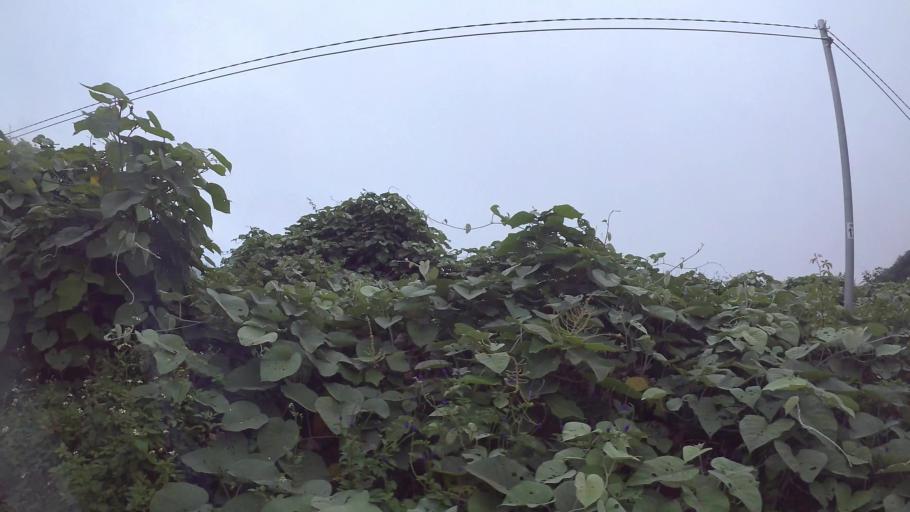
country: VN
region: Da Nang
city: Son Tra
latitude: 16.1152
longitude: 108.3075
